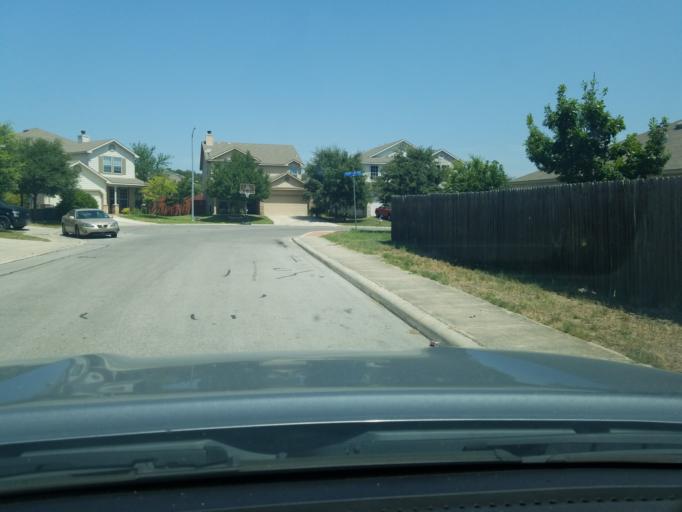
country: US
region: Texas
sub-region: Bexar County
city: Timberwood Park
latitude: 29.7006
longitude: -98.4844
